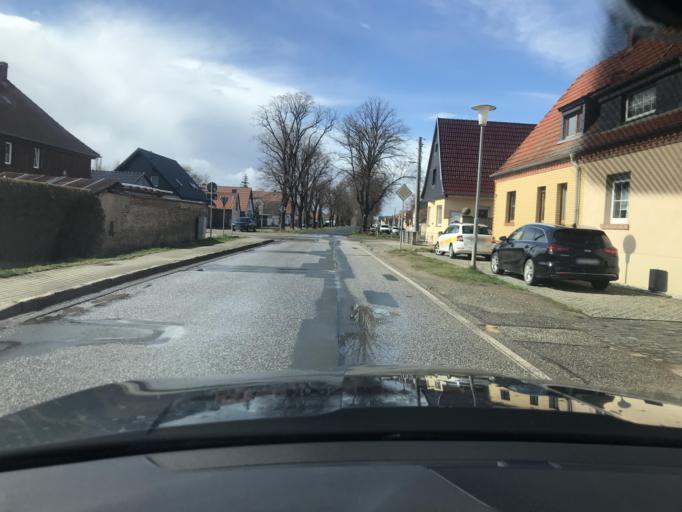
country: DE
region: Saxony-Anhalt
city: Nachterstedt
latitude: 51.7637
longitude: 11.3526
